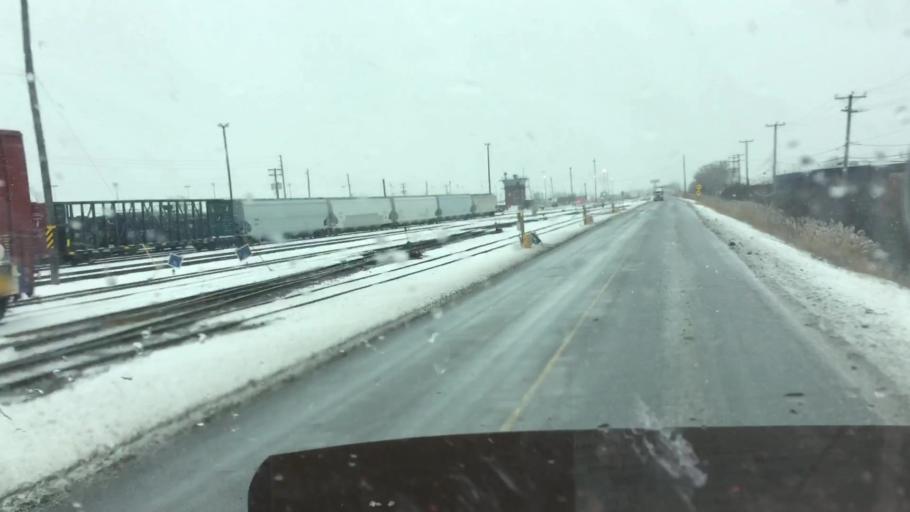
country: CA
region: Quebec
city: Cote-Saint-Luc
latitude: 45.4702
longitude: -73.6932
